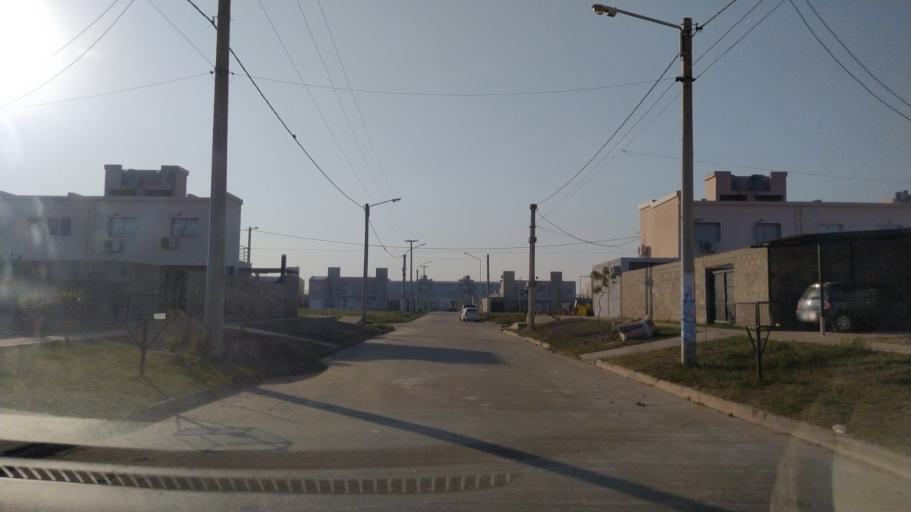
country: AR
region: Corrientes
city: Corrientes
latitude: -27.5229
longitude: -58.8060
